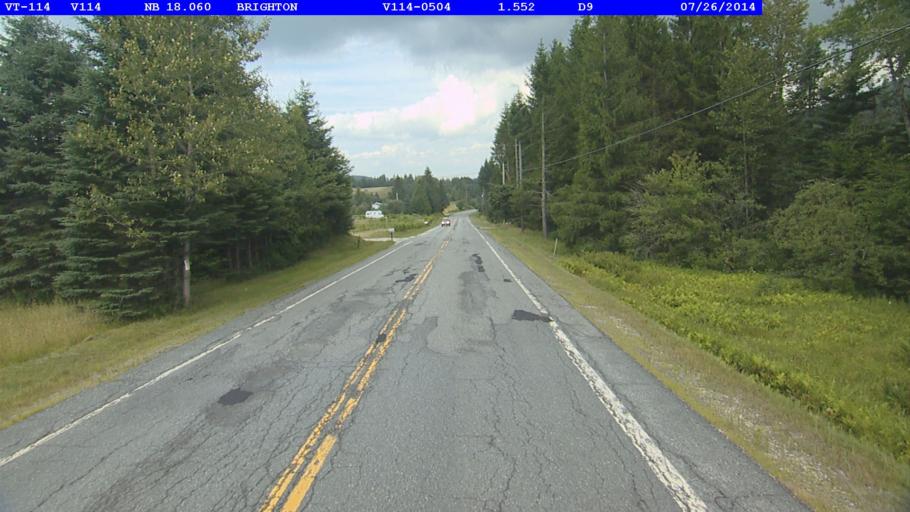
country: US
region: Vermont
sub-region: Caledonia County
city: Lyndonville
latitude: 44.7601
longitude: -71.8957
